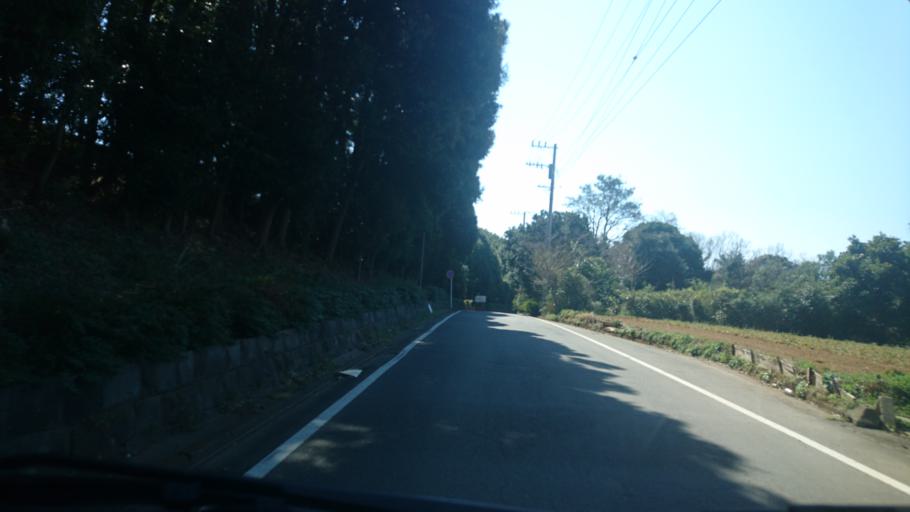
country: JP
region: Kanagawa
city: Fujisawa
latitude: 35.3885
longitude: 139.4252
